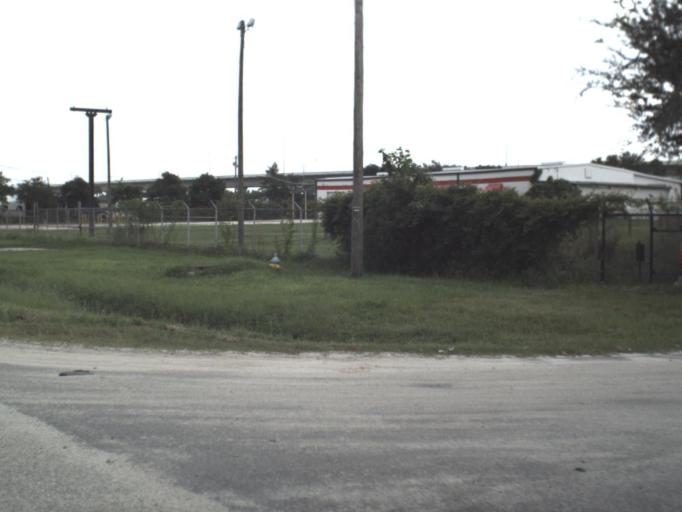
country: US
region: Florida
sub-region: Hillsborough County
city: Palm River-Clair Mel
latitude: 27.9520
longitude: -82.3897
